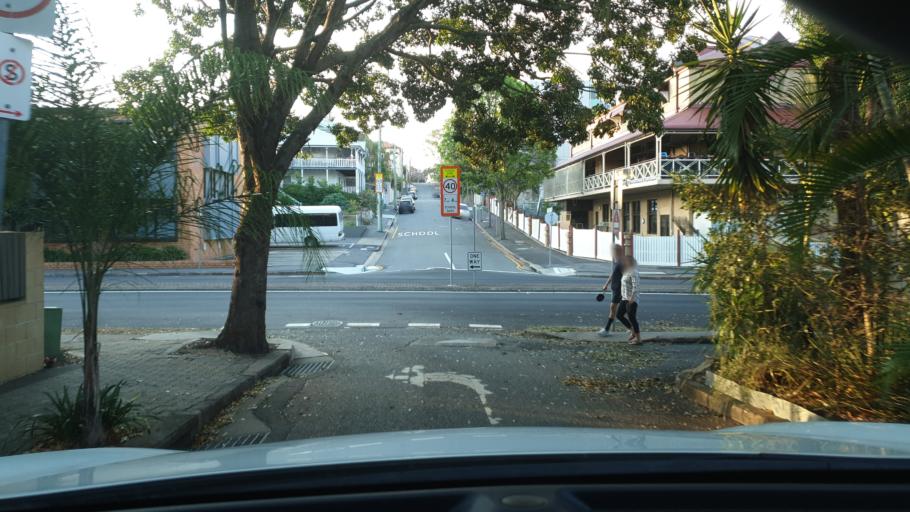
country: AU
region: Queensland
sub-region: Brisbane
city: Spring Hill
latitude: -27.4587
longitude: 153.0263
